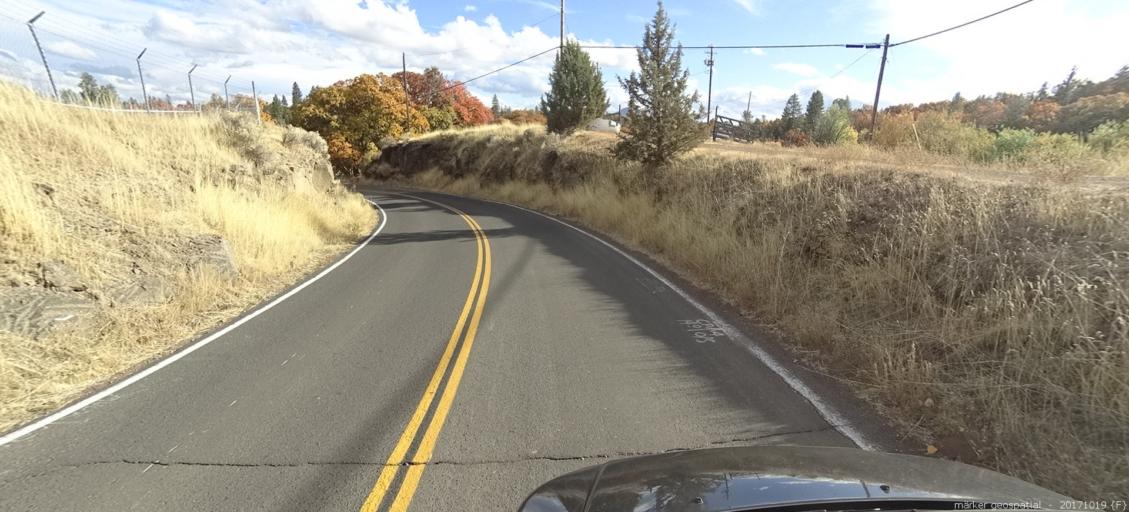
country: US
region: California
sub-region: Shasta County
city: Burney
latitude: 41.0014
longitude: -121.4377
